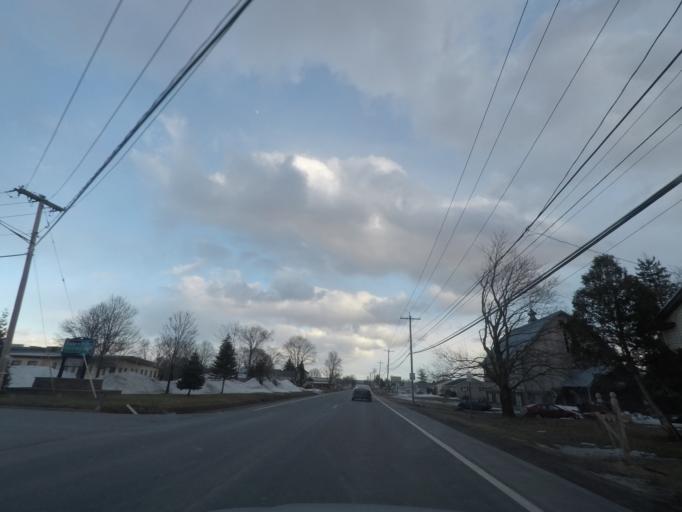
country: US
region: New York
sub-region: Oneida County
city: Utica
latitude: 43.1014
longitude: -75.1576
